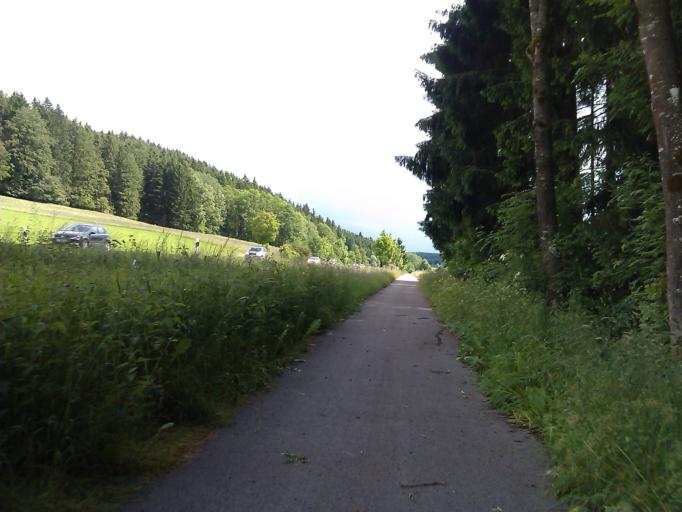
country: DE
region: Bavaria
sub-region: Swabia
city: Stotten am Auerberg
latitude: 47.7283
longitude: 10.6813
